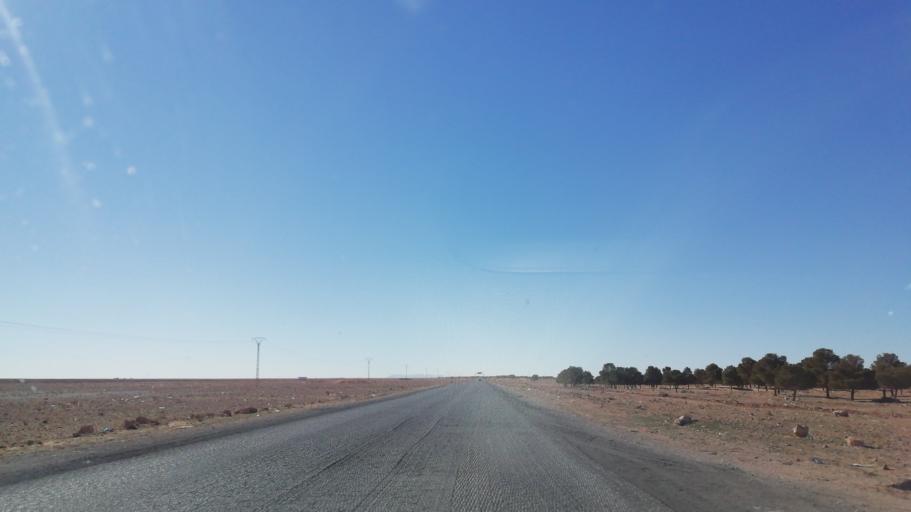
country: DZ
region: Saida
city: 'Ain el Hadjar
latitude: 34.0134
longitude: 0.0563
